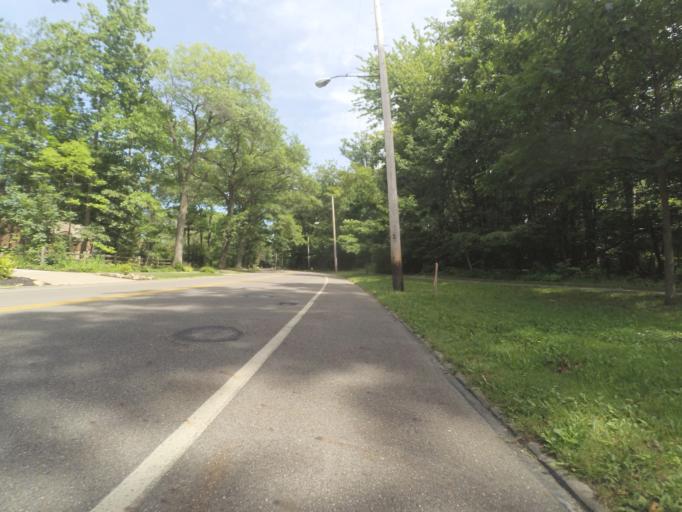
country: US
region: Ohio
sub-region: Cuyahoga County
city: University Heights
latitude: 41.4856
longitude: -81.5711
